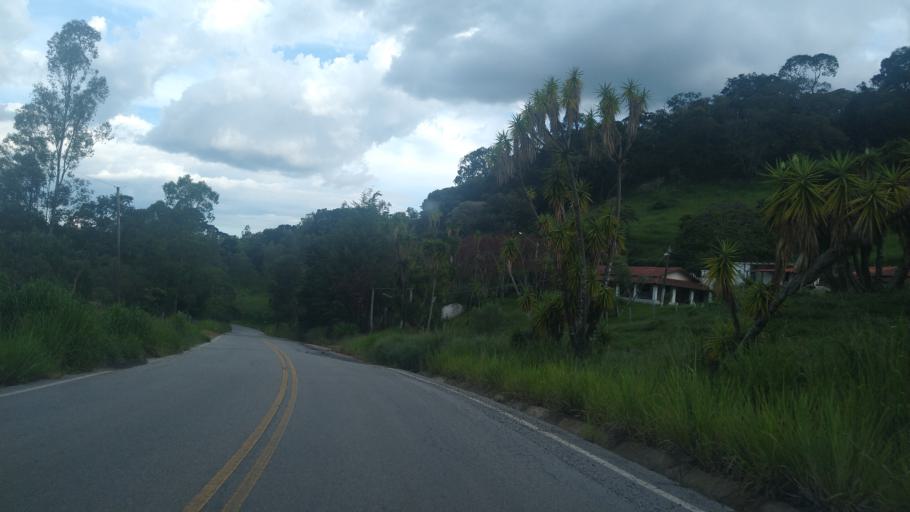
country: BR
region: Minas Gerais
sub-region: Extrema
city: Extrema
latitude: -22.7668
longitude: -46.3278
